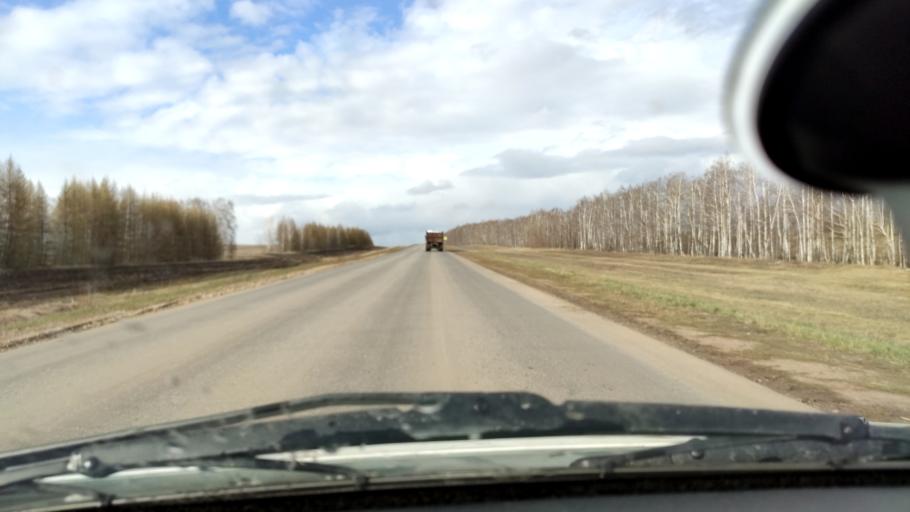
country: RU
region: Bashkortostan
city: Buzdyak
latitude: 54.6992
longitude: 54.5618
